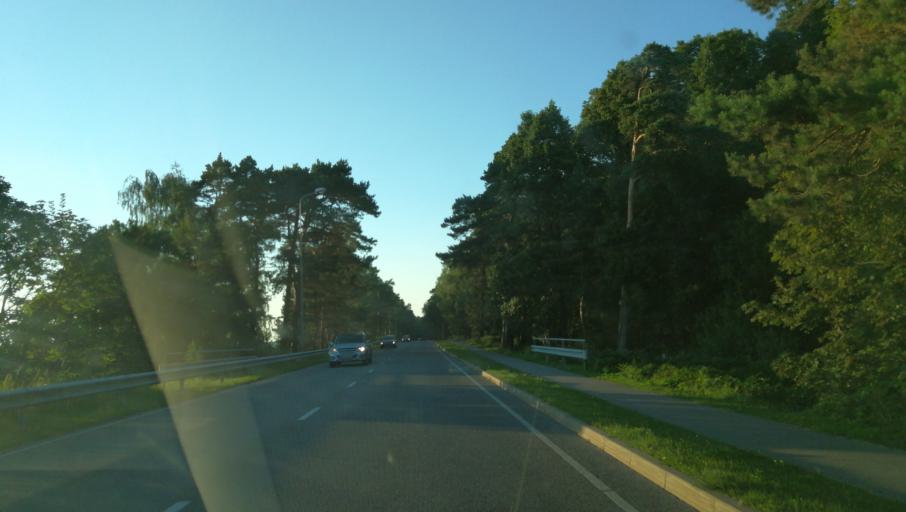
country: LV
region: Saulkrastu
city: Saulkrasti
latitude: 57.2875
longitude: 24.4128
